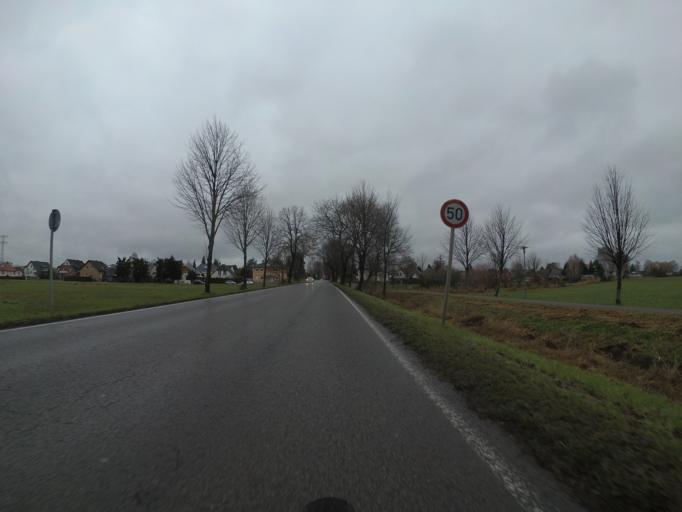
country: DE
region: Brandenburg
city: Ahrensfelde
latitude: 52.5654
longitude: 13.5916
